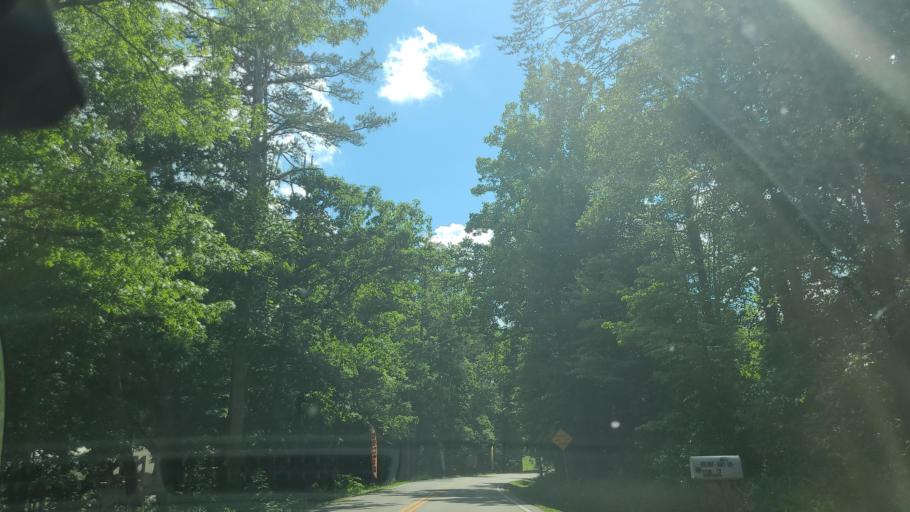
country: US
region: Kentucky
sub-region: Whitley County
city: Williamsburg
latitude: 36.8419
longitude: -84.2601
